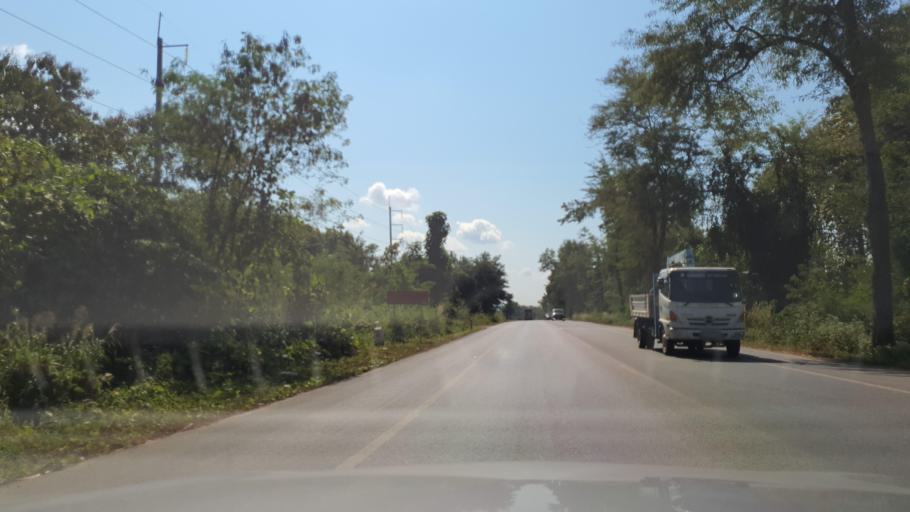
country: TH
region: Nan
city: Tha Wang Pha
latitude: 19.0759
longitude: 100.8086
